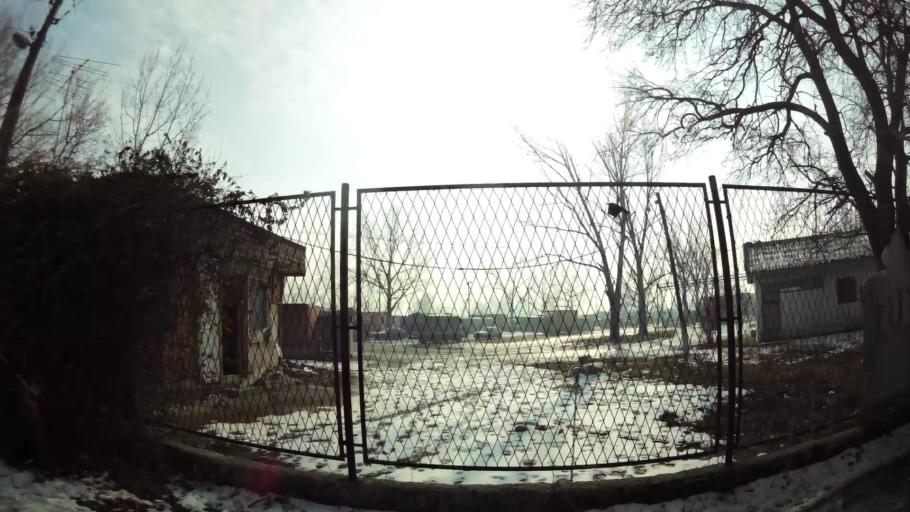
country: MK
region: Kisela Voda
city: Kisela Voda
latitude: 41.9914
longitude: 21.5023
